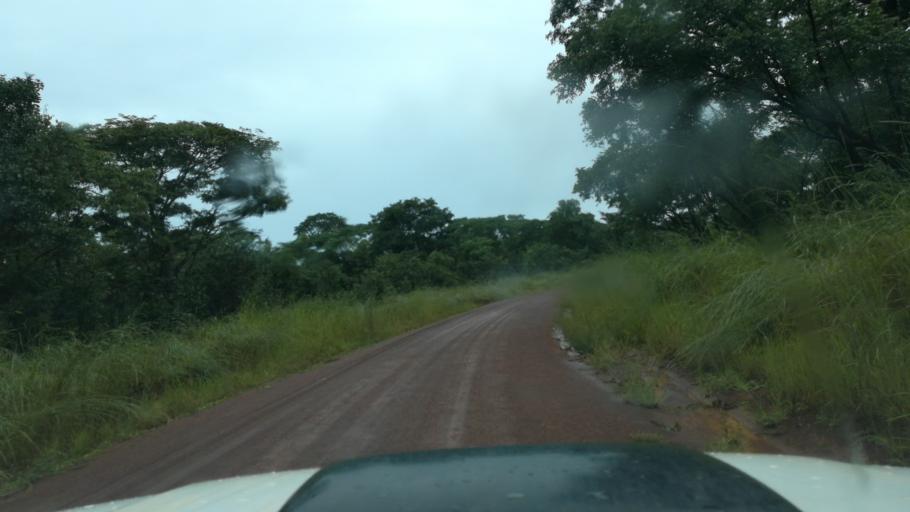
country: ZM
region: Luapula
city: Mwense
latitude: -10.3209
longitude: 28.1109
